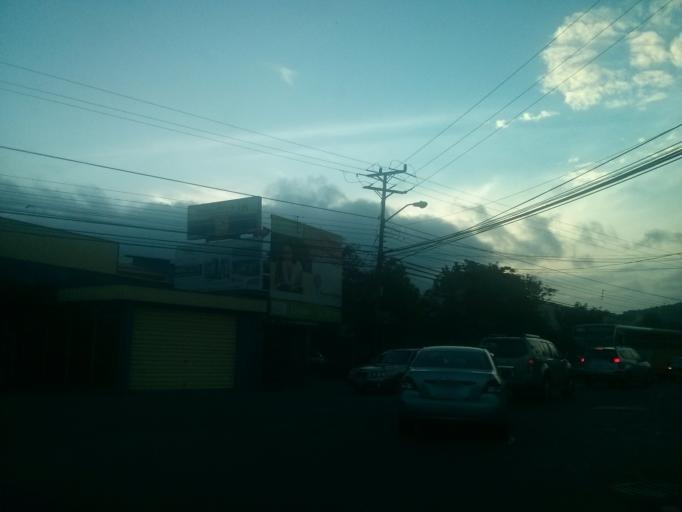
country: CR
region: Cartago
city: Cartago
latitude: 9.8811
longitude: -83.9354
